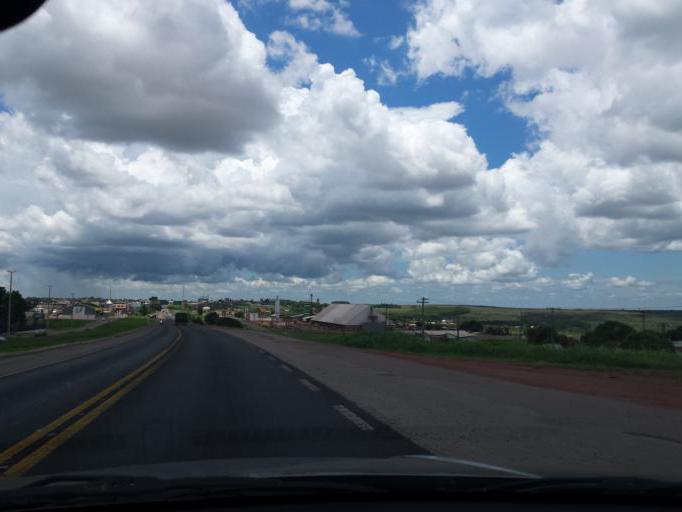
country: BR
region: Goias
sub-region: Cristalina
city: Cristalina
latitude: -16.7580
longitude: -47.6096
